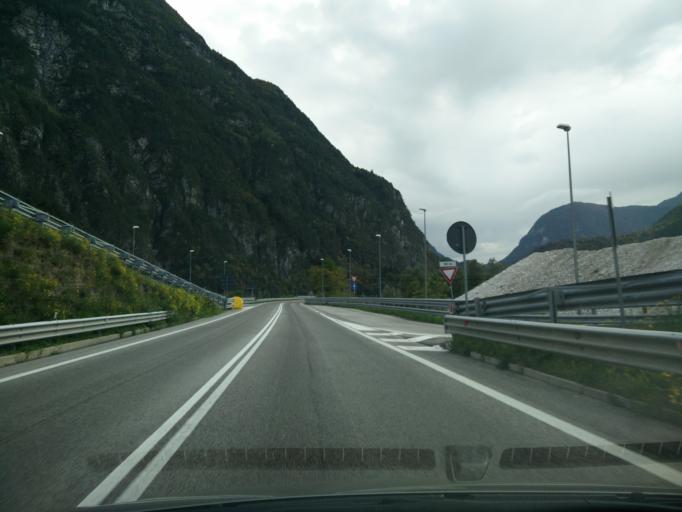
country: IT
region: Veneto
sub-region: Provincia di Belluno
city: Ospitale di Cadore
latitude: 46.3539
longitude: 12.3382
